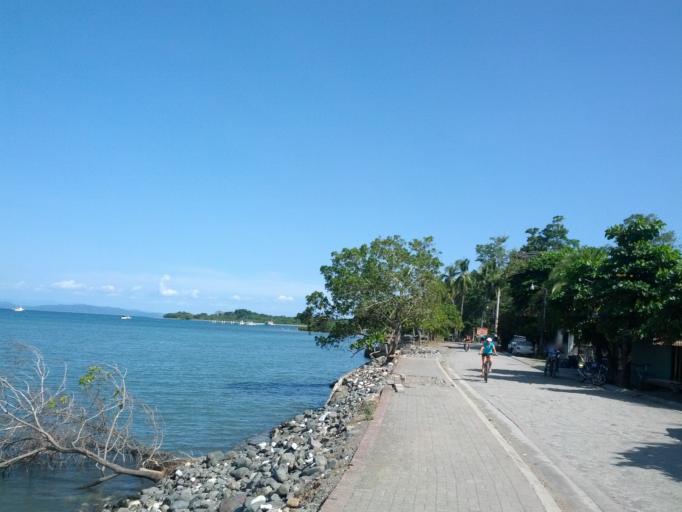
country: CR
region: Puntarenas
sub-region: Canton de Golfito
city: Golfito
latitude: 8.5406
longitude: -83.3029
